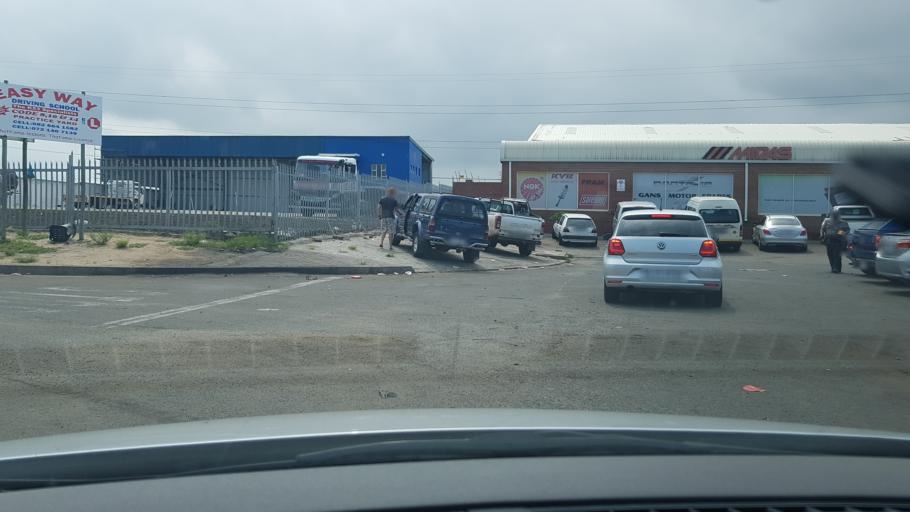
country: ZA
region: KwaZulu-Natal
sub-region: uThungulu District Municipality
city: Richards Bay
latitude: -28.7442
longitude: 32.0491
